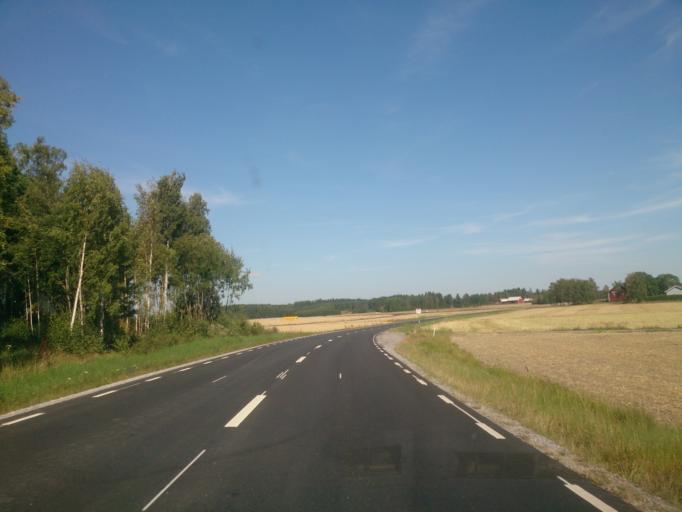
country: SE
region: OEstergoetland
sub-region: Norrkopings Kommun
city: Krokek
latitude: 58.5794
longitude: 16.5273
